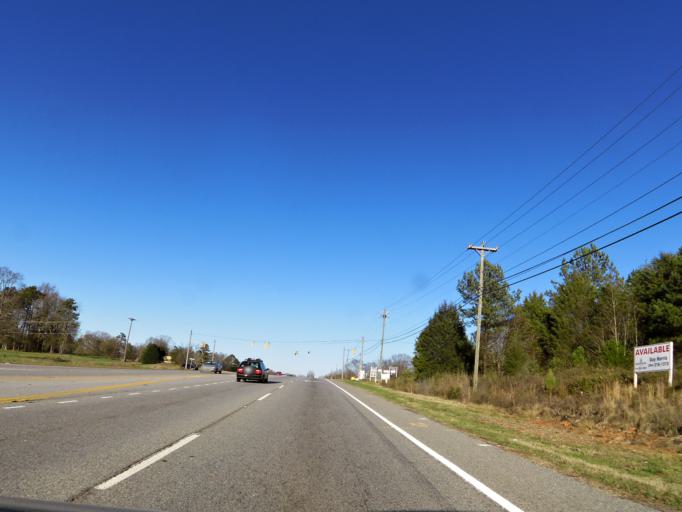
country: US
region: South Carolina
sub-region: Spartanburg County
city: Fairforest
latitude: 34.8992
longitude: -82.0366
